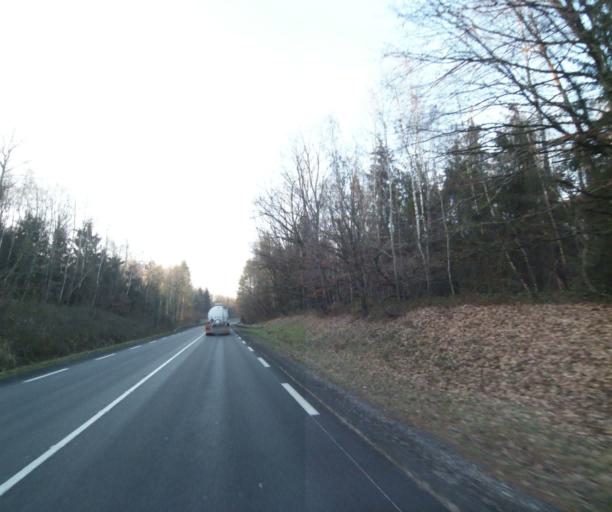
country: FR
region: Champagne-Ardenne
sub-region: Departement de la Haute-Marne
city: Bienville
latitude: 48.5637
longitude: 5.0391
